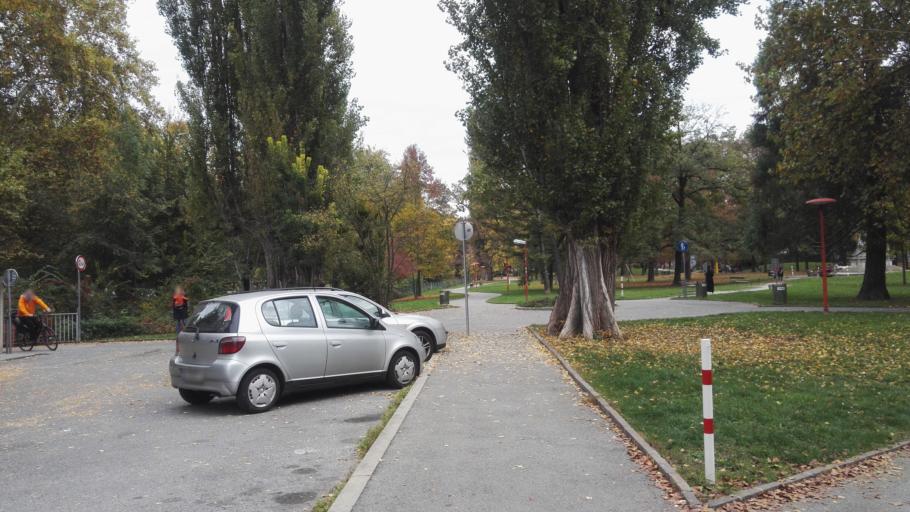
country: AT
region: Styria
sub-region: Graz Stadt
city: Graz
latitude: 47.0731
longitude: 15.4251
